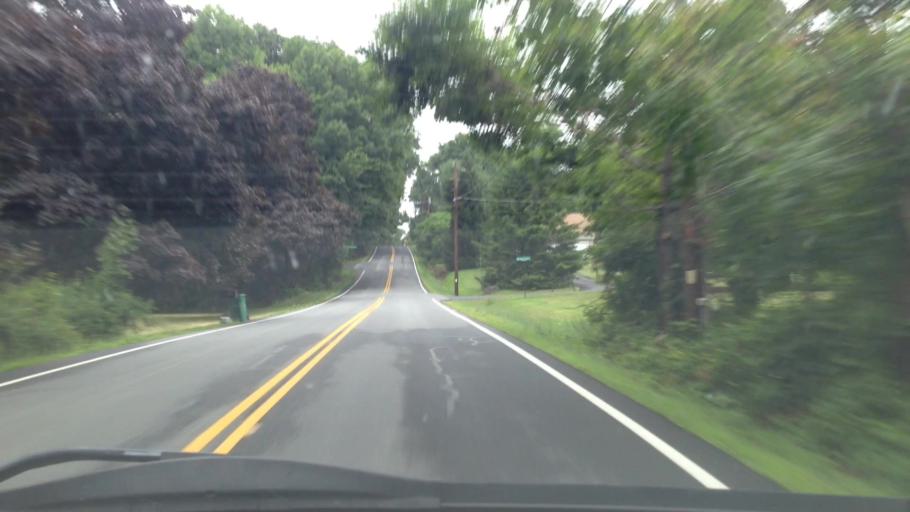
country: US
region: New York
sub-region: Ulster County
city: New Paltz
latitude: 41.7618
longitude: -74.0585
